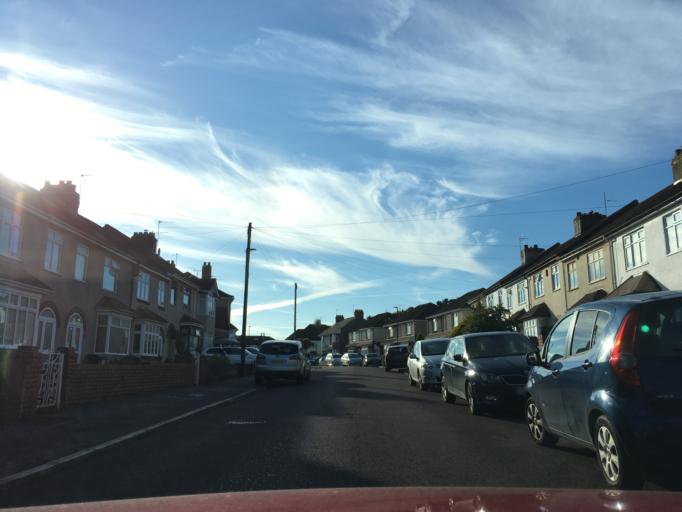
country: GB
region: England
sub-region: South Gloucestershire
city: Mangotsfield
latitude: 51.4840
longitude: -2.5027
